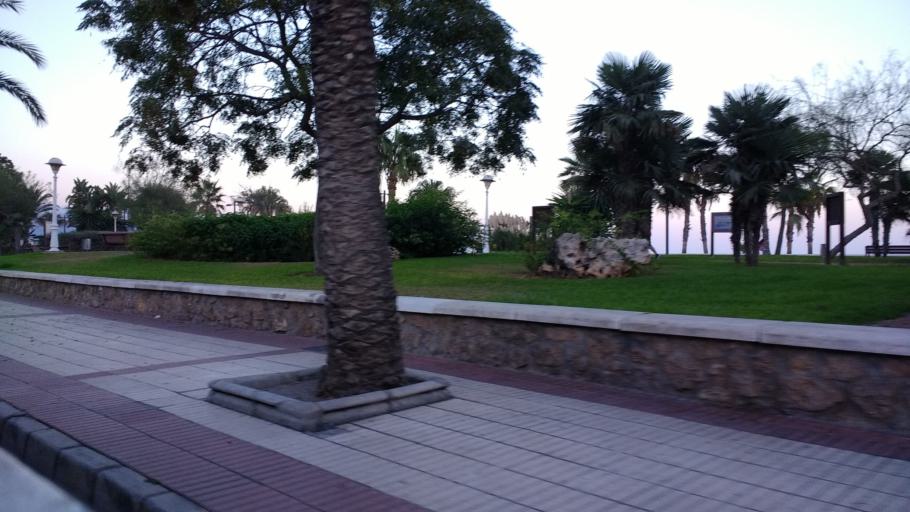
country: ES
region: Andalusia
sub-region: Provincia de Malaga
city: Velez-Malaga
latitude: 36.7406
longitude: -4.0910
